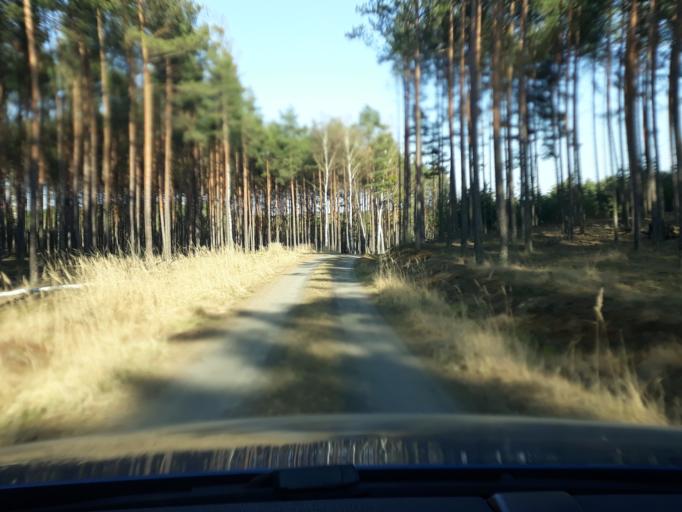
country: PL
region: Pomeranian Voivodeship
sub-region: Powiat bytowski
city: Lipnica
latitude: 53.9137
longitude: 17.4837
